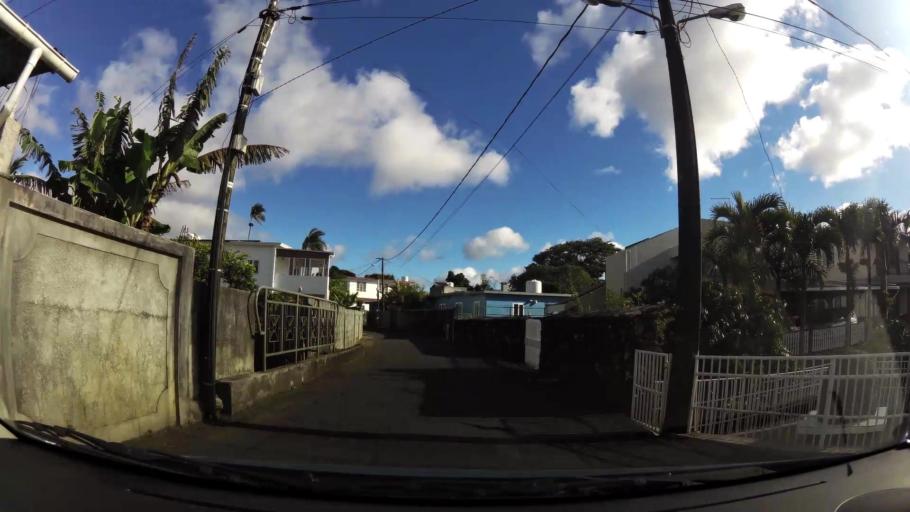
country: MU
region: Plaines Wilhems
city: Curepipe
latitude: -20.2920
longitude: 57.5198
